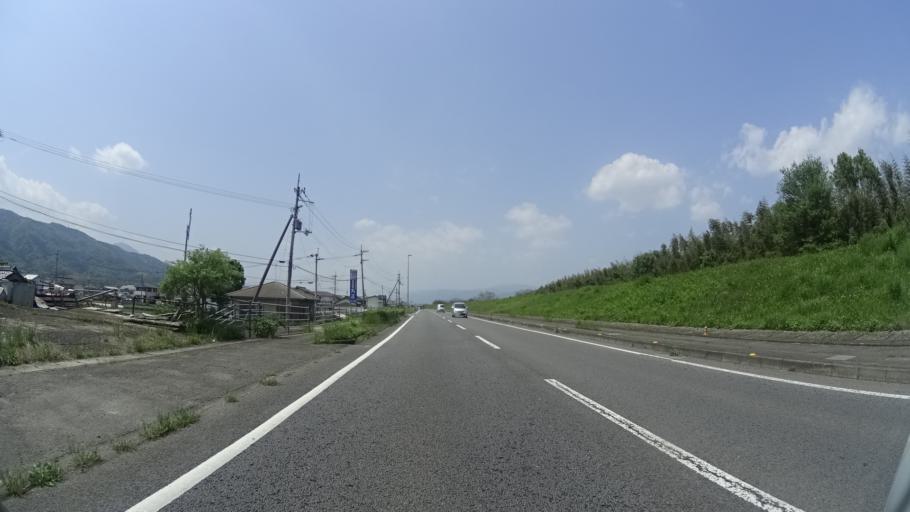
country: JP
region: Tokushima
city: Kamojimacho-jogejima
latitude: 34.0622
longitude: 134.2911
